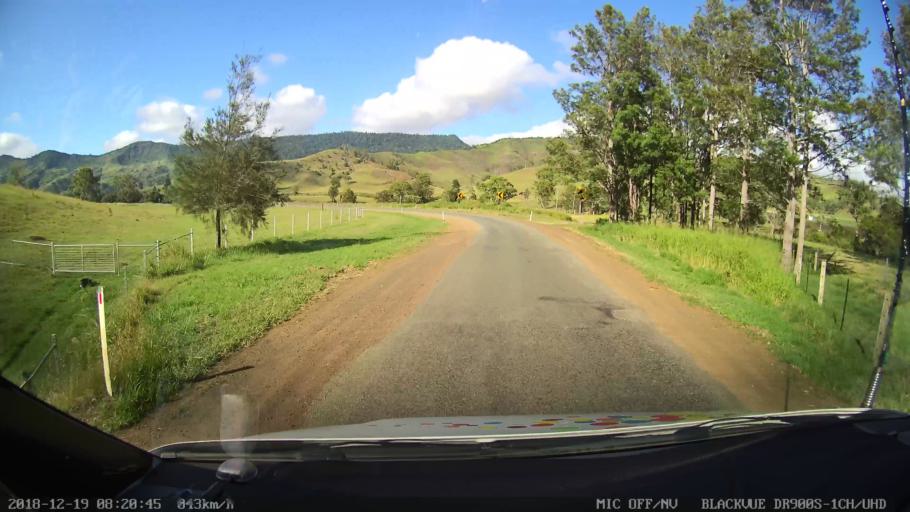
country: AU
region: New South Wales
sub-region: Kyogle
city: Kyogle
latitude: -28.2922
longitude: 152.9095
